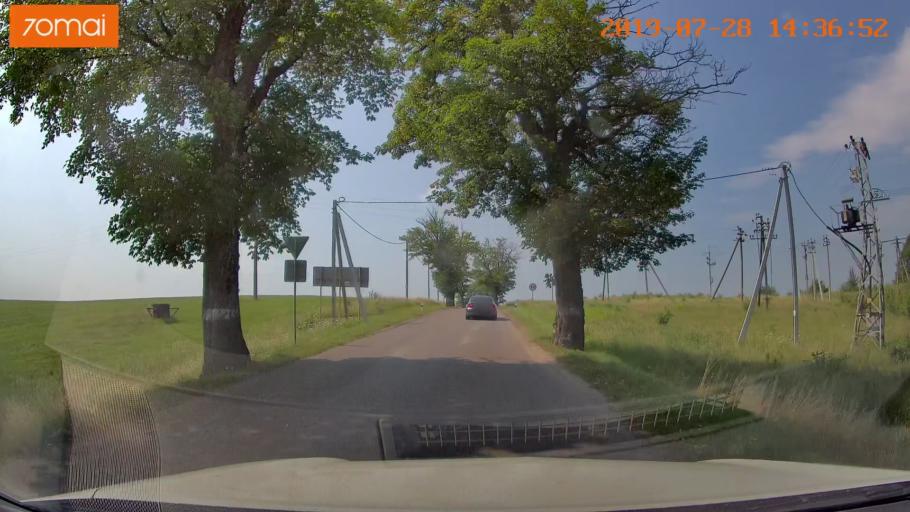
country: RU
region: Kaliningrad
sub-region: Gorod Kaliningrad
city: Yantarnyy
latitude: 54.8398
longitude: 20.0053
